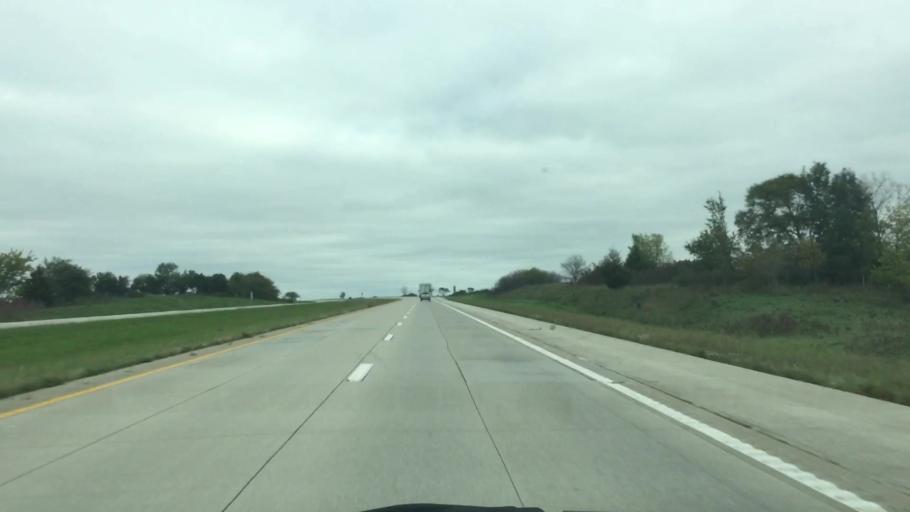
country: US
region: Missouri
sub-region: Daviess County
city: Gallatin
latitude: 39.9705
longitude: -94.0965
